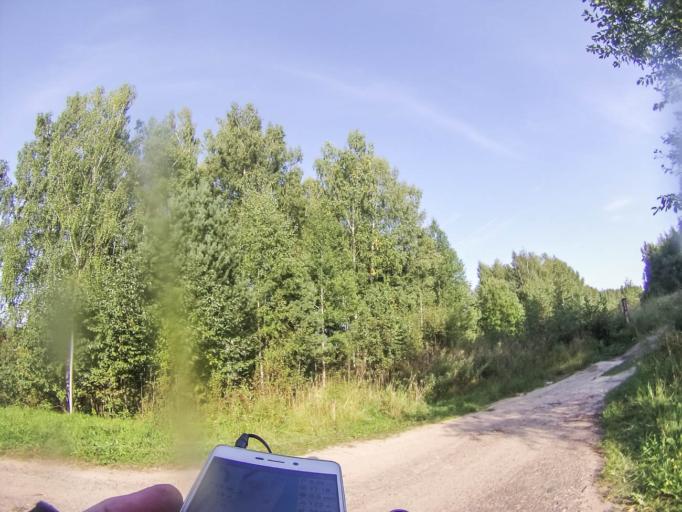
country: RU
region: Jaroslavl
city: Myshkin
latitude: 57.7217
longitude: 38.4140
